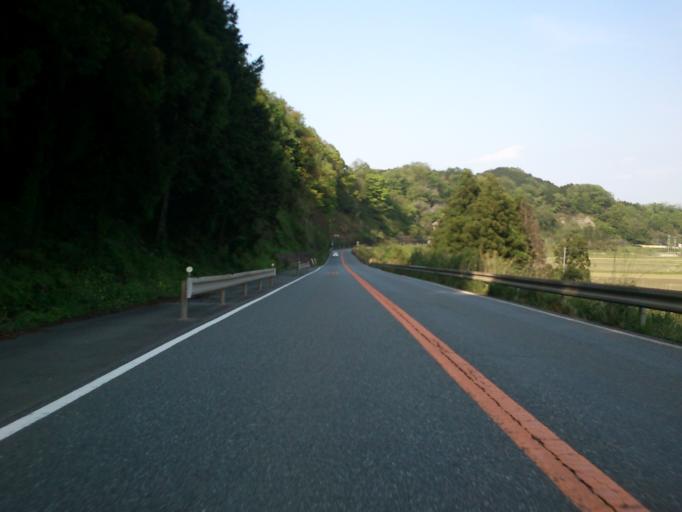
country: JP
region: Kyoto
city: Fukuchiyama
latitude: 35.3217
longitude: 135.0136
